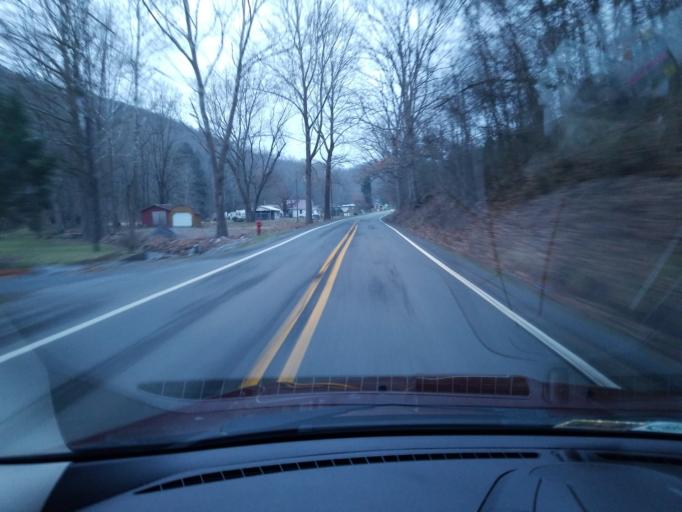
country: US
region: West Virginia
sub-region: Greenbrier County
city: Ronceverte
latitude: 37.7523
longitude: -80.4063
